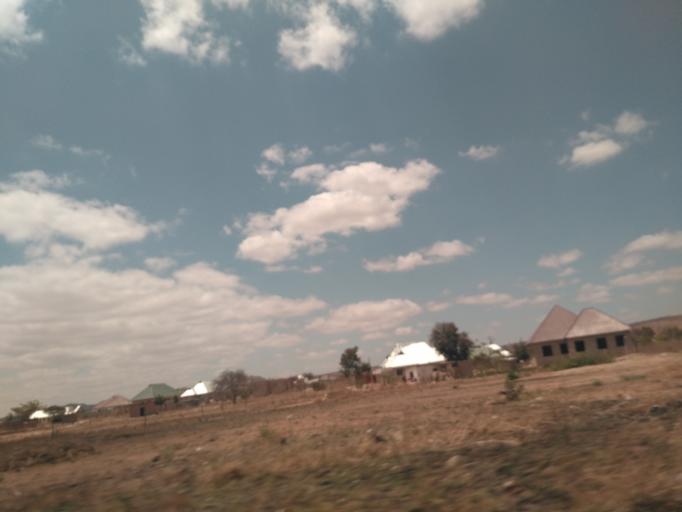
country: TZ
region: Dodoma
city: Kisasa
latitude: -6.1711
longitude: 35.7908
